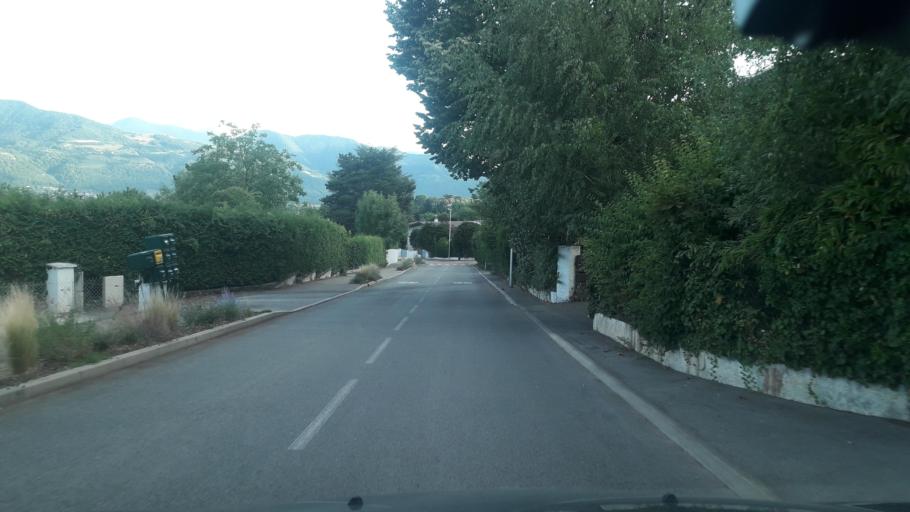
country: FR
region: Rhone-Alpes
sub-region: Departement de l'Isere
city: Biviers
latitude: 45.2364
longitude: 5.8052
